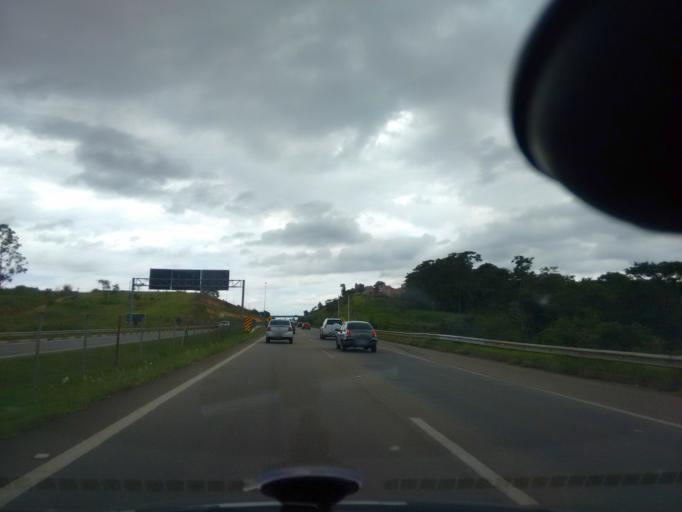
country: BR
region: Sao Paulo
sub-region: Indaiatuba
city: Indaiatuba
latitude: -23.0327
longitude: -47.1324
